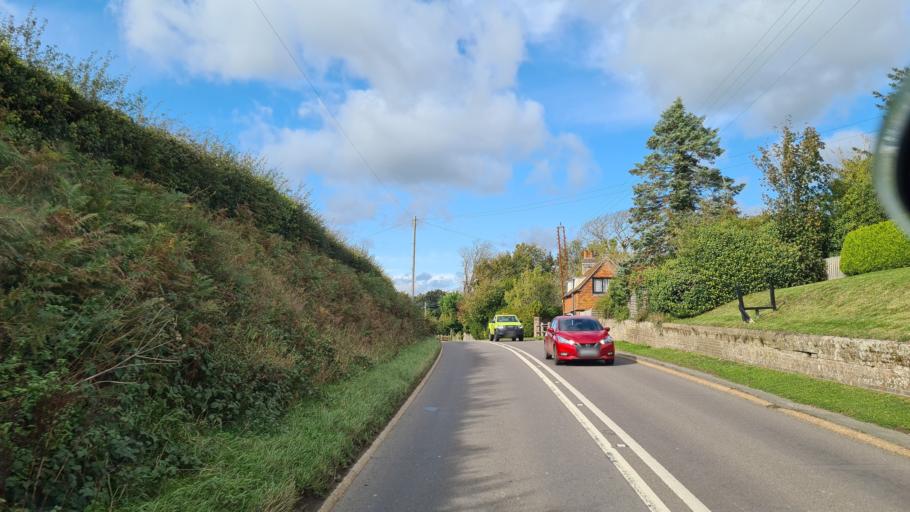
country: GB
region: England
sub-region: East Sussex
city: Bodle Street
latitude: 50.8800
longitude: 0.3597
